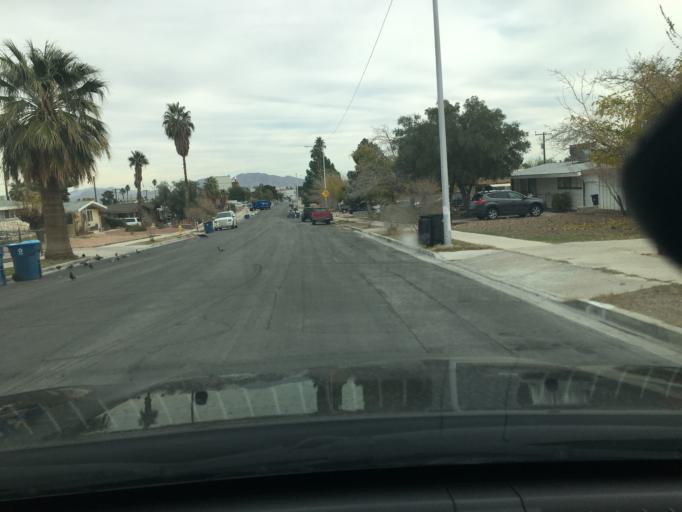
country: US
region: Nevada
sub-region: Clark County
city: Spring Valley
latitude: 36.1631
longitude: -115.2149
